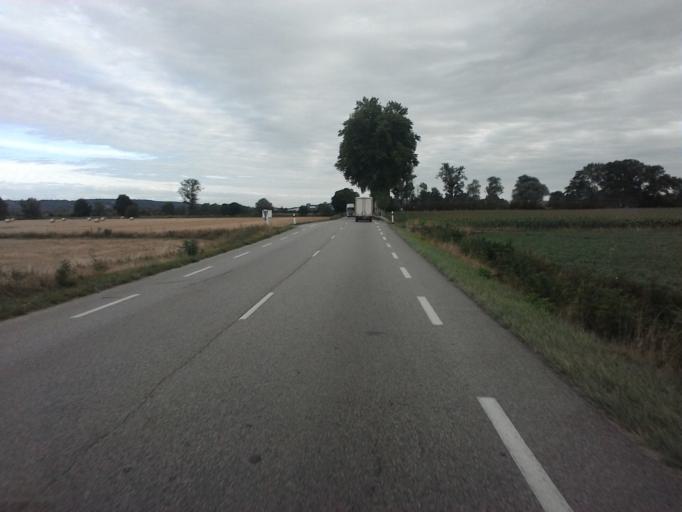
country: FR
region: Rhone-Alpes
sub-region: Departement de l'Ain
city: Ambronay
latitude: 46.0014
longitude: 5.3420
